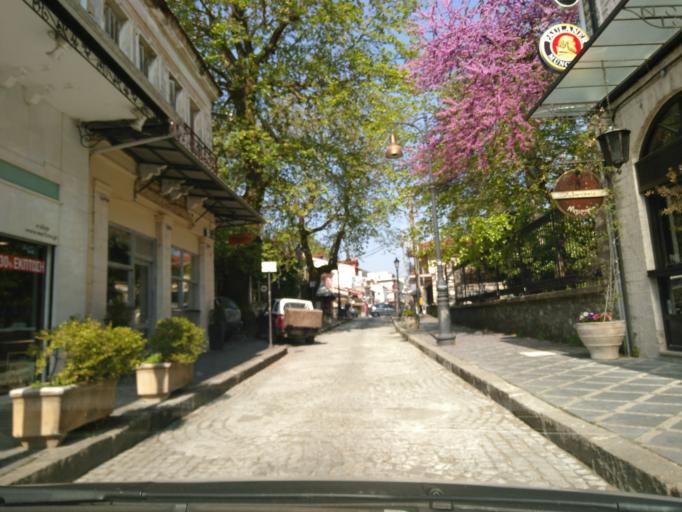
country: GR
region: Epirus
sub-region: Nomos Ioanninon
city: Ioannina
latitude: 39.6704
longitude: 20.8513
